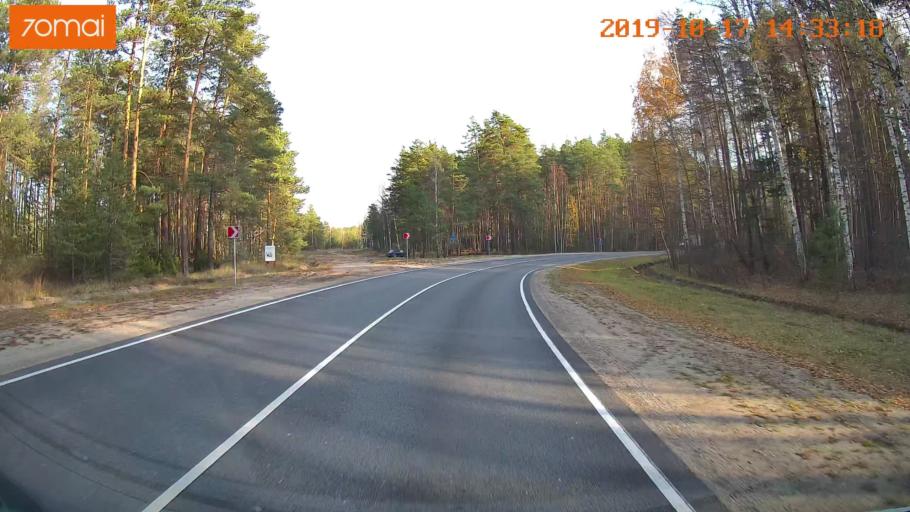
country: RU
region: Rjazan
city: Solotcha
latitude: 54.9243
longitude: 39.9959
